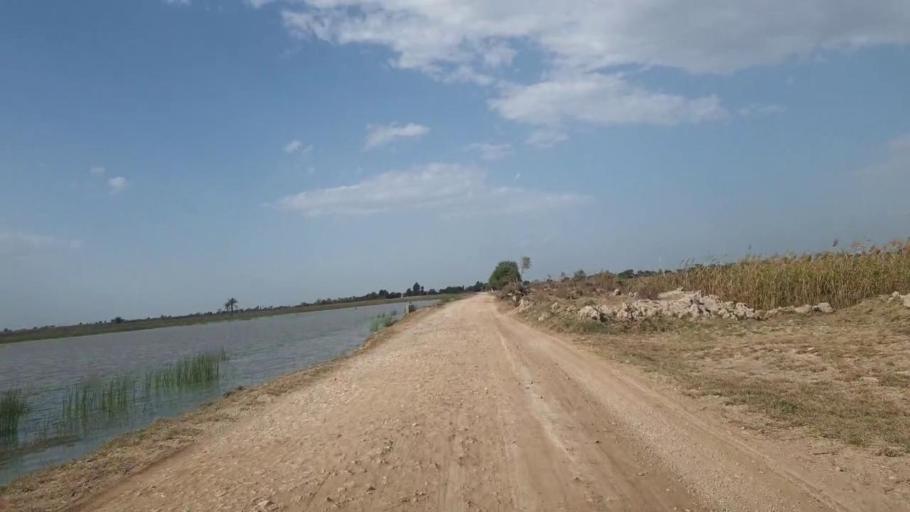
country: PK
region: Sindh
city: Shahdadpur
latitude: 25.9984
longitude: 68.4620
